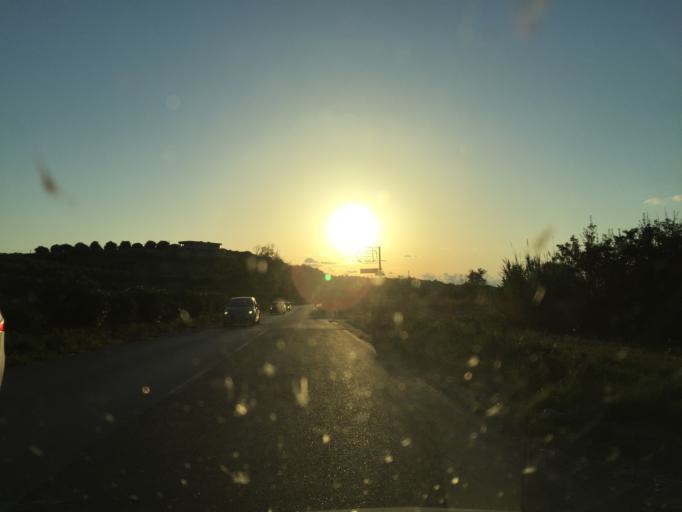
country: IT
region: Calabria
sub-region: Provincia di Vibo-Valentia
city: Pannaconi
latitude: 38.7158
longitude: 16.0593
